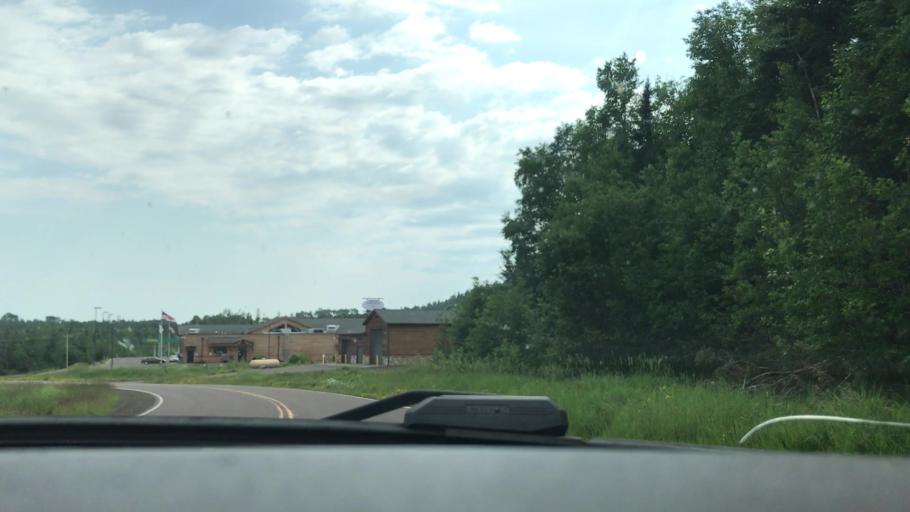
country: CA
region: Ontario
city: Neebing
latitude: 47.9555
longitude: -89.6939
